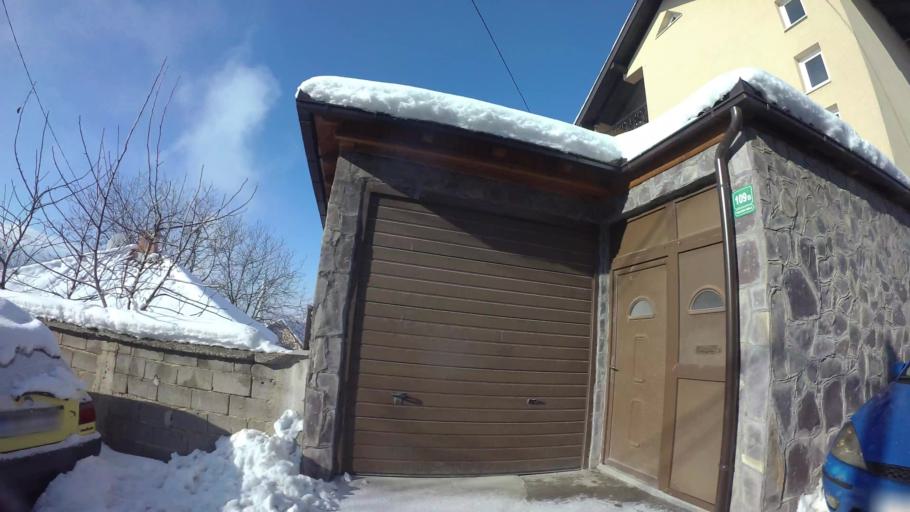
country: BA
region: Federation of Bosnia and Herzegovina
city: Kobilja Glava
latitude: 43.8769
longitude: 18.4224
